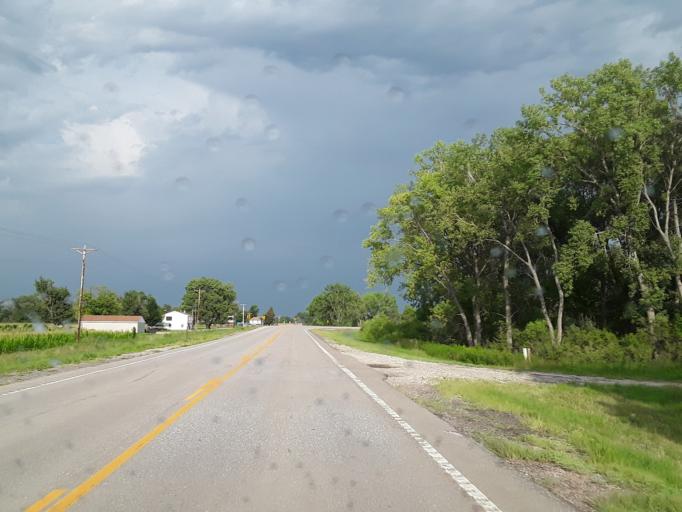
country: US
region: Nebraska
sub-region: Saunders County
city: Ashland
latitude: 41.0886
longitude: -96.3770
